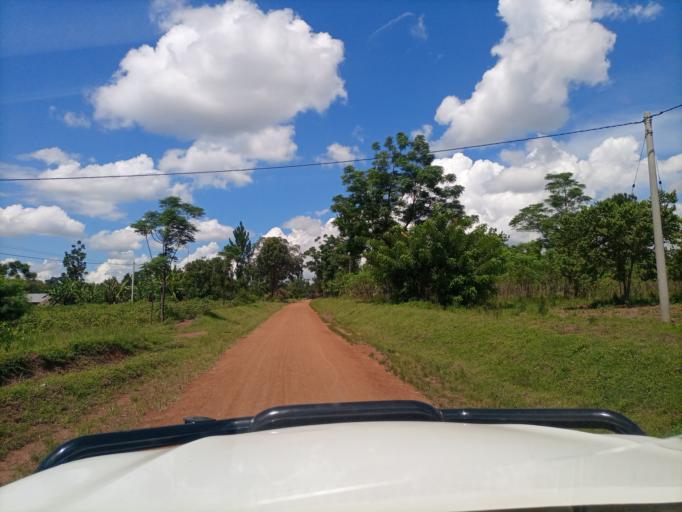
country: UG
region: Eastern Region
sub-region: Tororo District
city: Tororo
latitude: 0.7015
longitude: 34.0132
